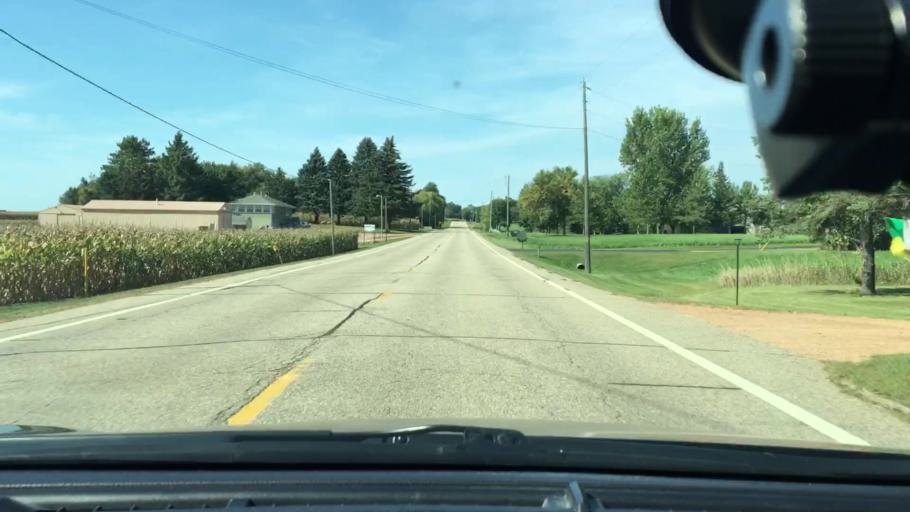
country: US
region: Minnesota
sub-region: Hennepin County
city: Corcoran
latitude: 45.1124
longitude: -93.5743
